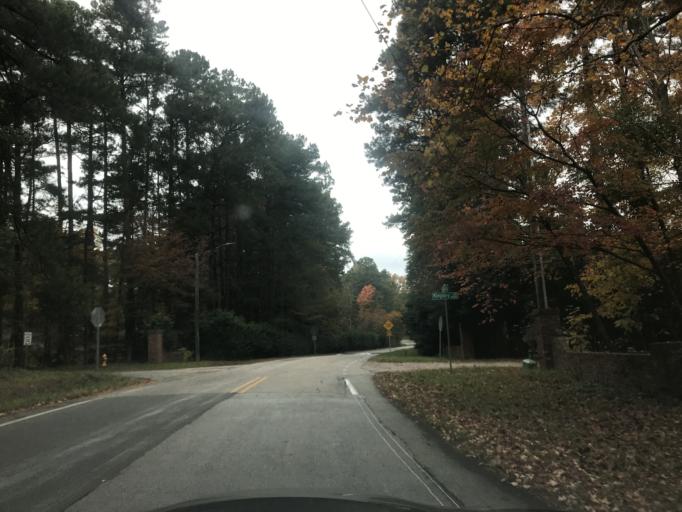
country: US
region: North Carolina
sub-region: Wake County
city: West Raleigh
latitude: 35.8527
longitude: -78.6756
